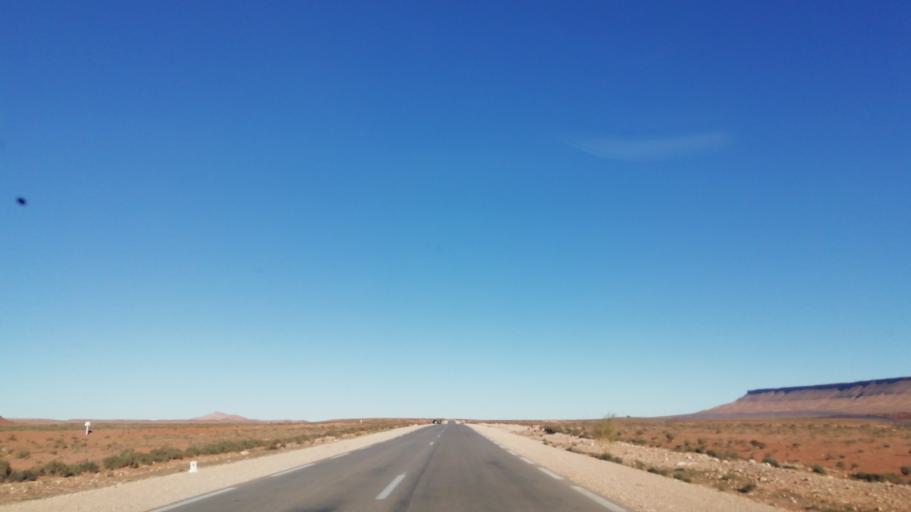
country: DZ
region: El Bayadh
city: El Abiodh Sidi Cheikh
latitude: 33.0885
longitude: 0.1861
